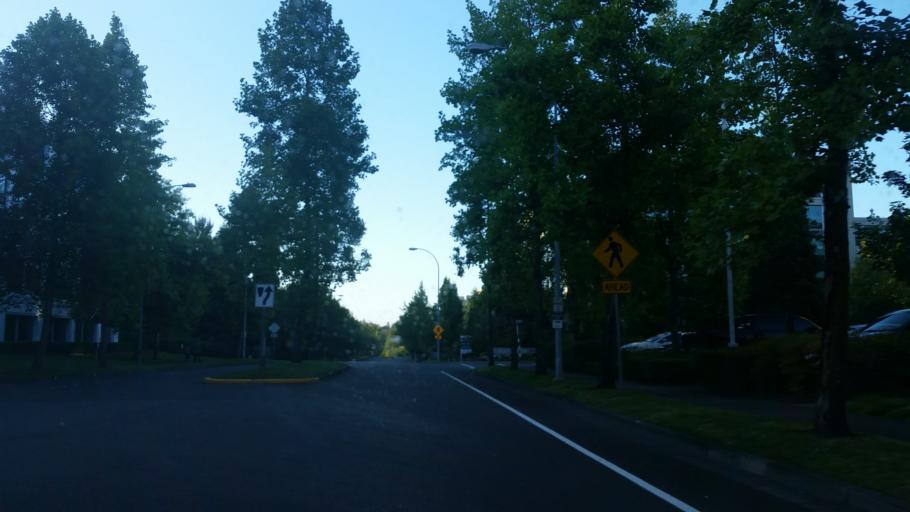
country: US
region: Washington
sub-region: King County
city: Eastgate
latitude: 47.5808
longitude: -122.1548
